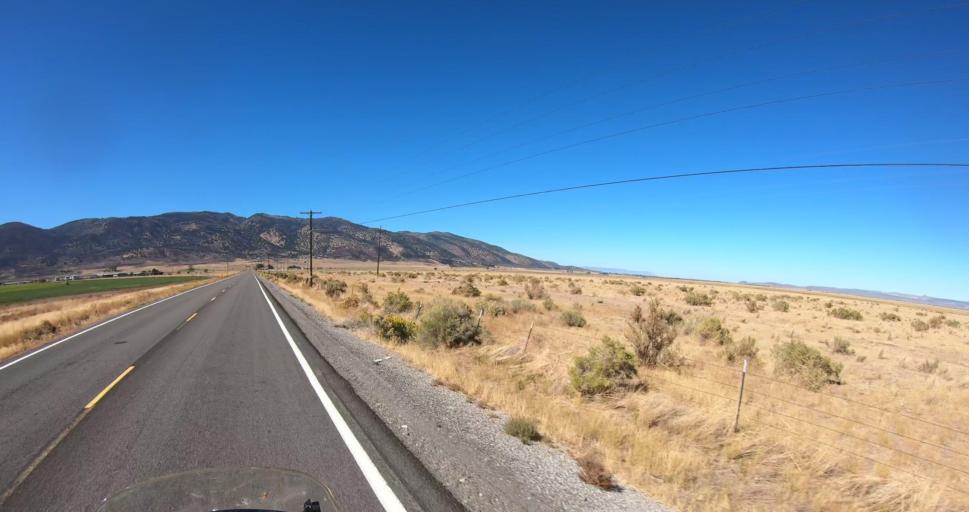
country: US
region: Oregon
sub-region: Lake County
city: Lakeview
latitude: 42.6152
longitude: -120.4765
